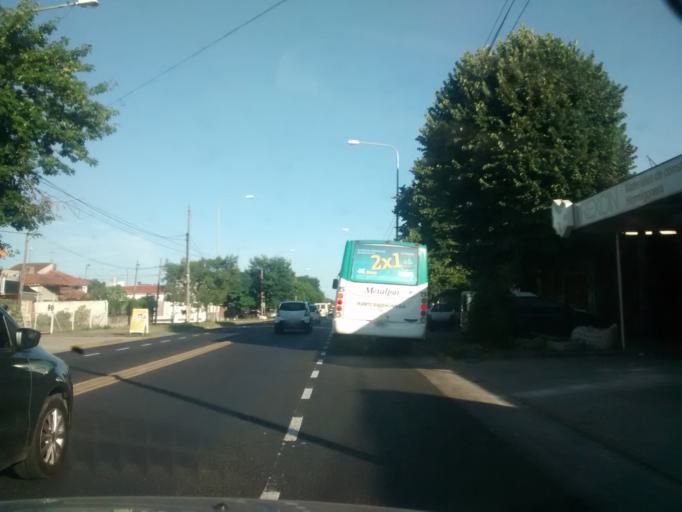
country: AR
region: Buenos Aires
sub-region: Partido de La Plata
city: La Plata
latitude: -34.8995
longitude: -57.9374
